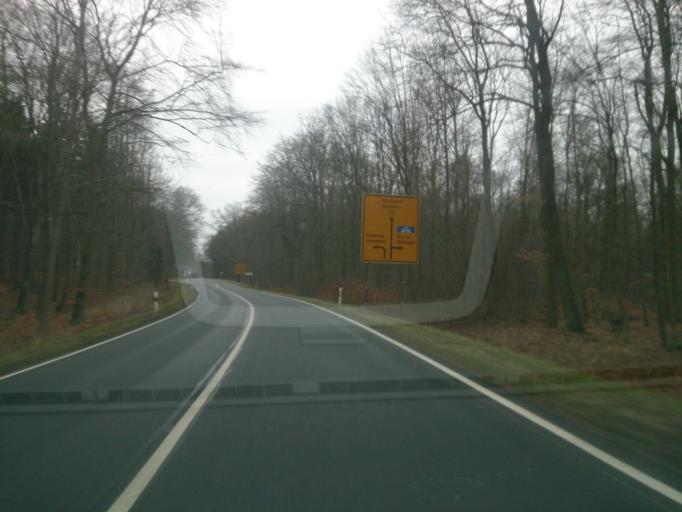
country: DE
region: Mecklenburg-Vorpommern
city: Borrentin
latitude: 53.7598
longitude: 12.9361
